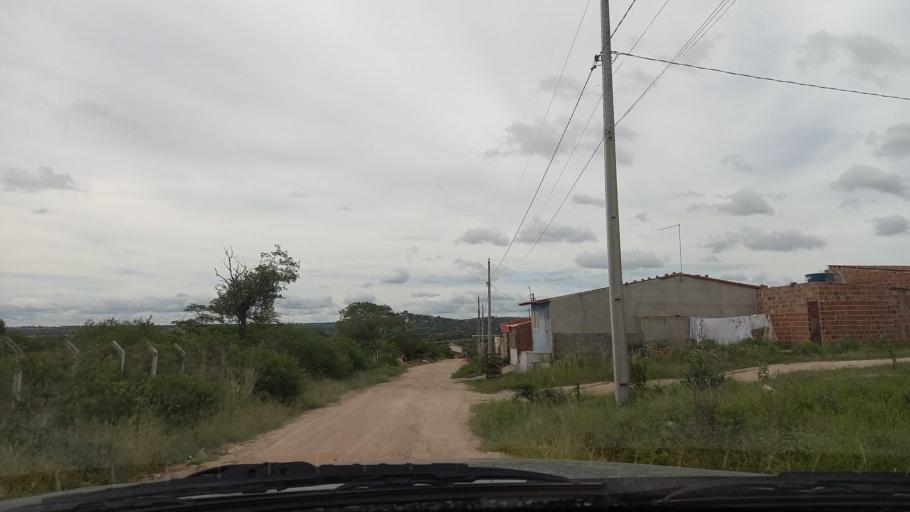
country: BR
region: Pernambuco
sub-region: Gravata
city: Gravata
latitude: -8.2185
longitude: -35.6089
